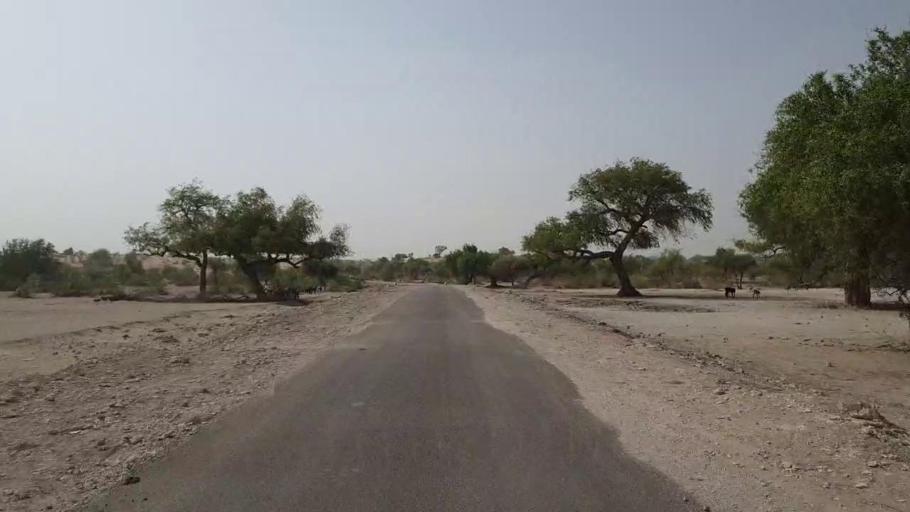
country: PK
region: Sindh
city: Mithi
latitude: 24.6165
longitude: 69.9190
